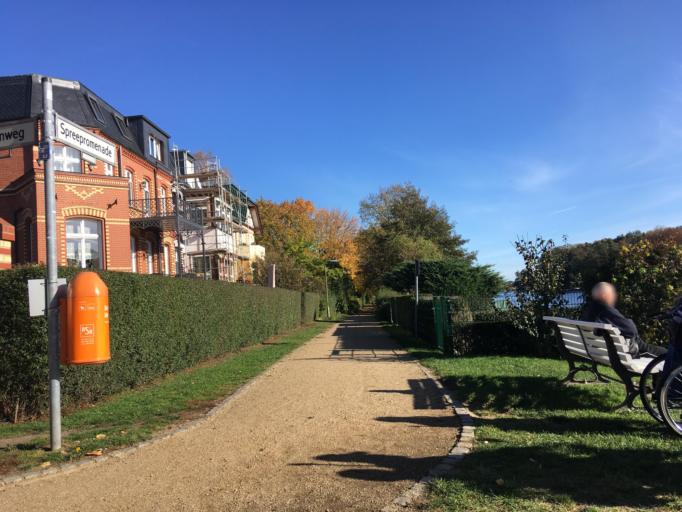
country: DE
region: Berlin
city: Berlin Koepenick
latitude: 52.4504
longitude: 13.5962
